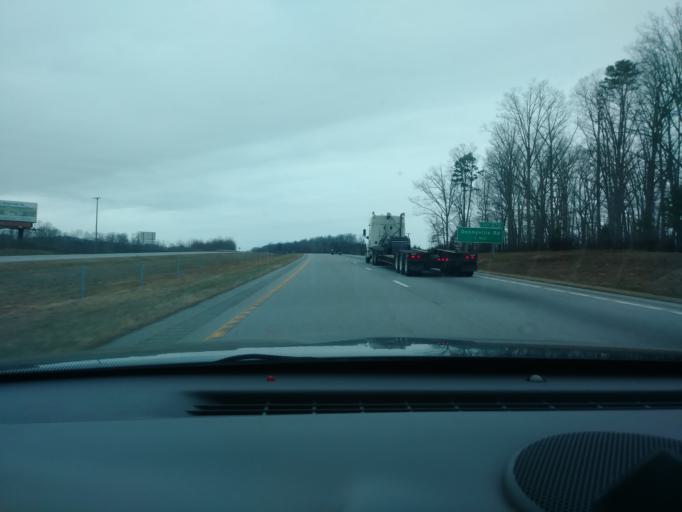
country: US
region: North Carolina
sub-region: Yadkin County
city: Jonesville
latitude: 36.1413
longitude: -80.8746
